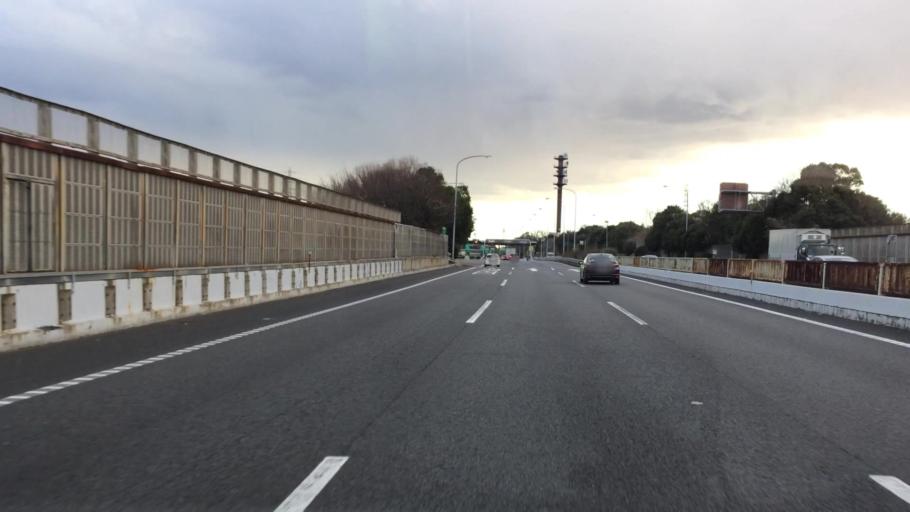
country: JP
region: Kanagawa
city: Yokohama
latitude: 35.4863
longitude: 139.5928
